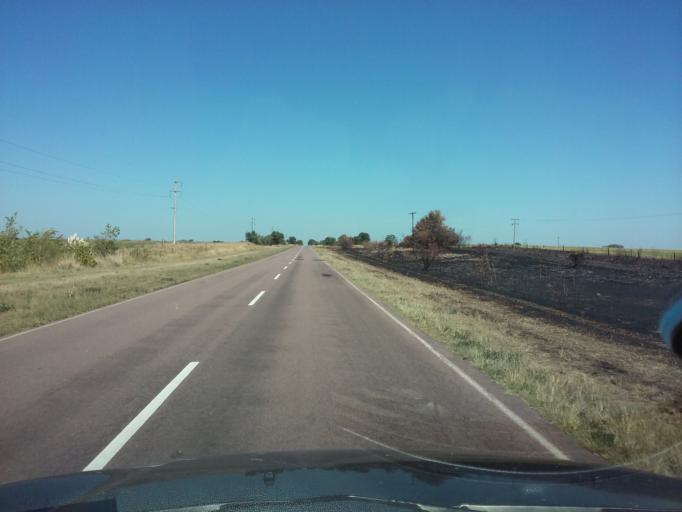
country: AR
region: La Pampa
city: Uriburu
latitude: -36.3888
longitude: -63.9432
